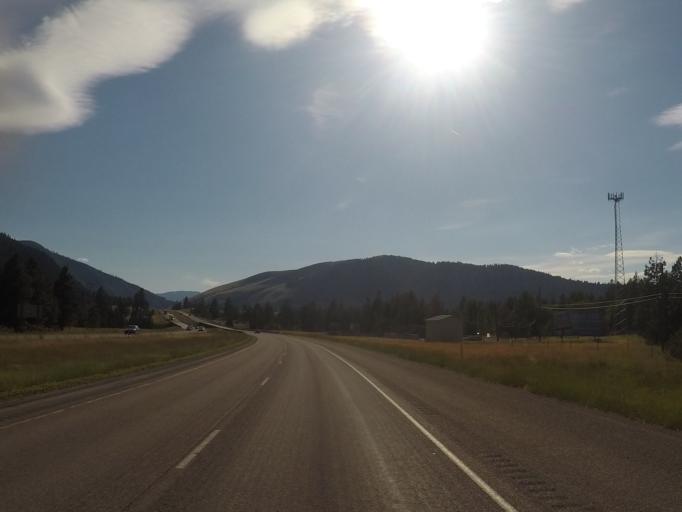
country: US
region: Montana
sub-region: Missoula County
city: Bonner-West Riverside
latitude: 46.8793
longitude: -113.9047
